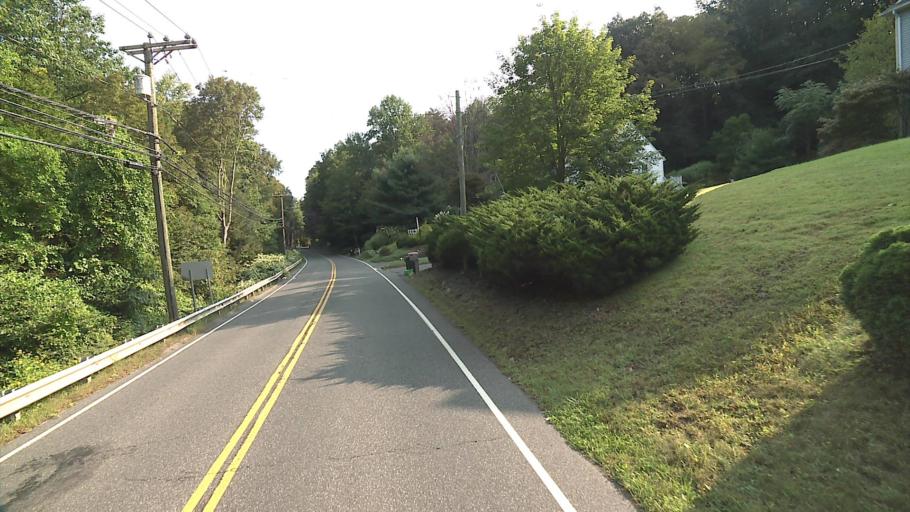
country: US
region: Connecticut
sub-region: Fairfield County
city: Newtown
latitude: 41.4280
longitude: -73.2802
